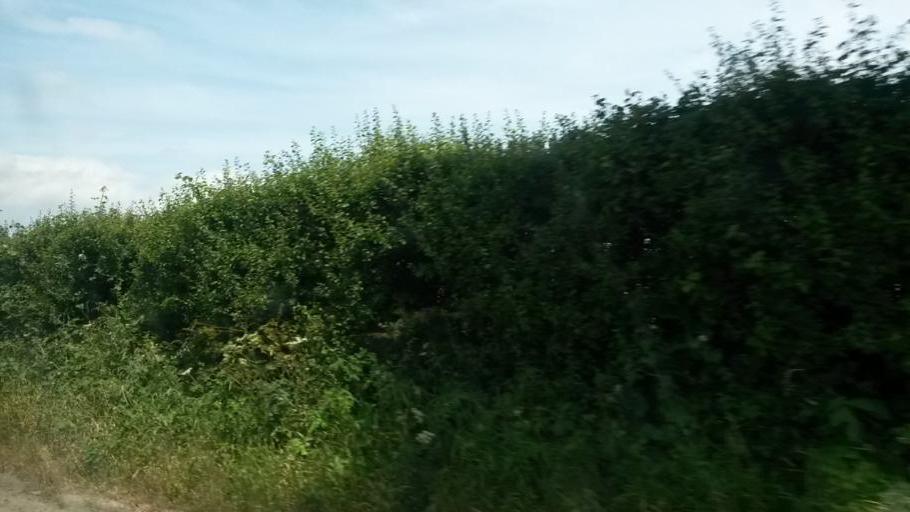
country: IE
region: Leinster
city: Lusk
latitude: 53.5434
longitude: -6.2037
